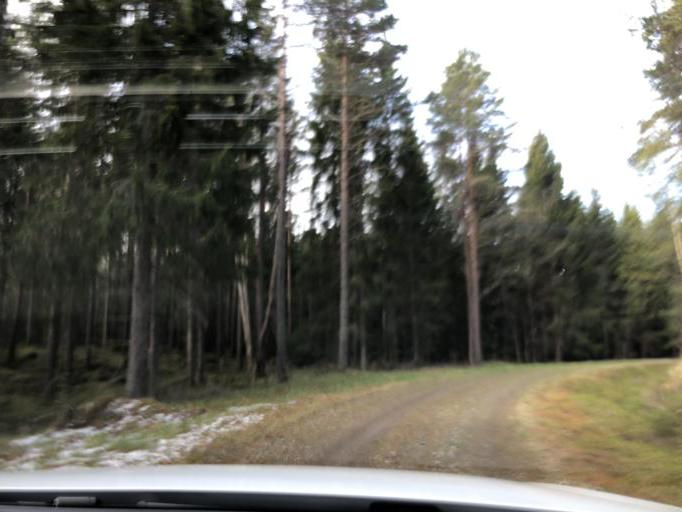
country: SE
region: Uppsala
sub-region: Heby Kommun
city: Tarnsjo
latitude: 60.2940
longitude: 16.8275
